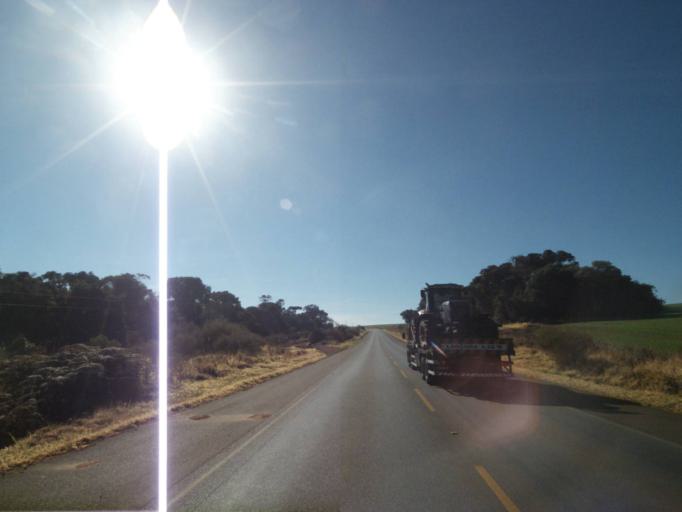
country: BR
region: Parana
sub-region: Tibagi
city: Tibagi
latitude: -24.4625
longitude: -50.4321
